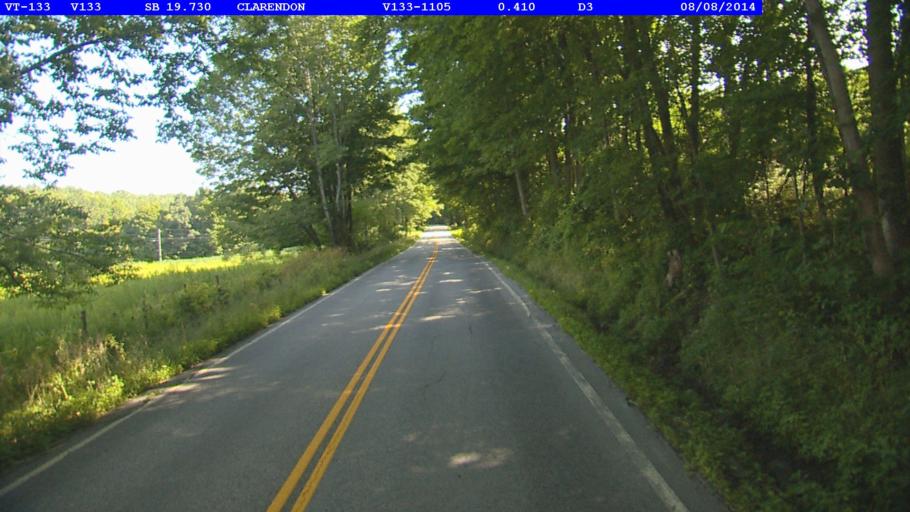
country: US
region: Vermont
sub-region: Rutland County
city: West Rutland
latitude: 43.5567
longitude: -73.0364
